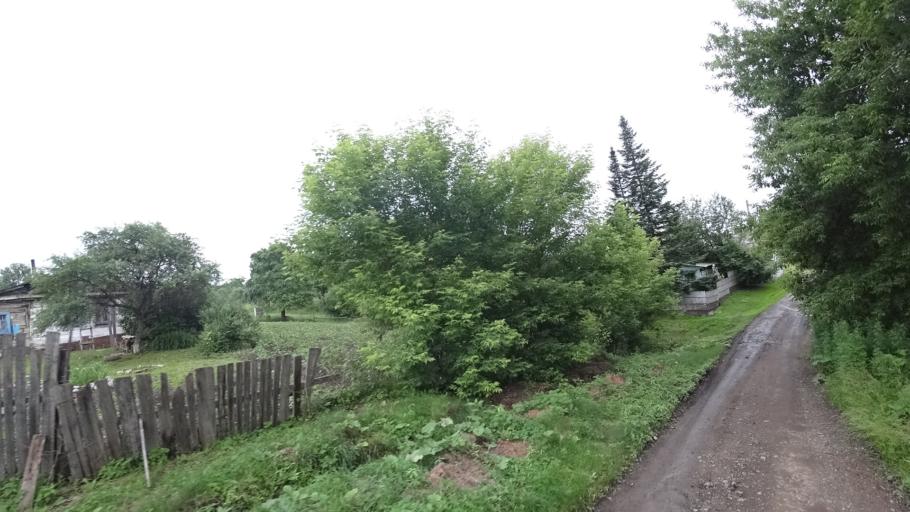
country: RU
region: Primorskiy
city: Novosysoyevka
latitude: 44.2242
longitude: 133.3543
